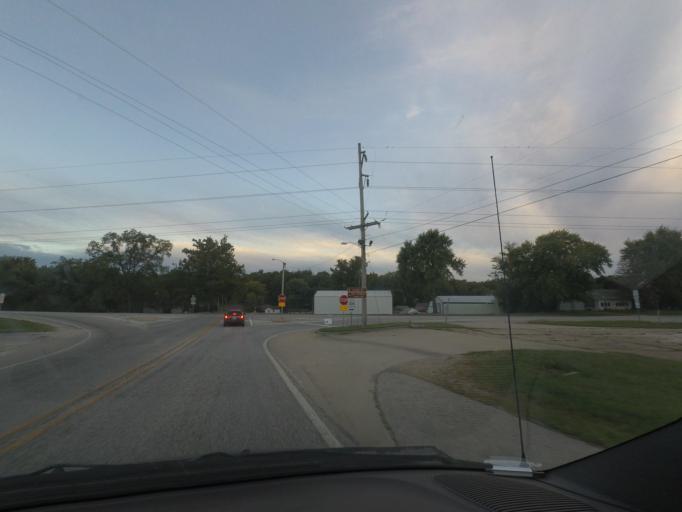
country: US
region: Illinois
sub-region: Pike County
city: Barry
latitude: 39.7003
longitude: -91.0393
